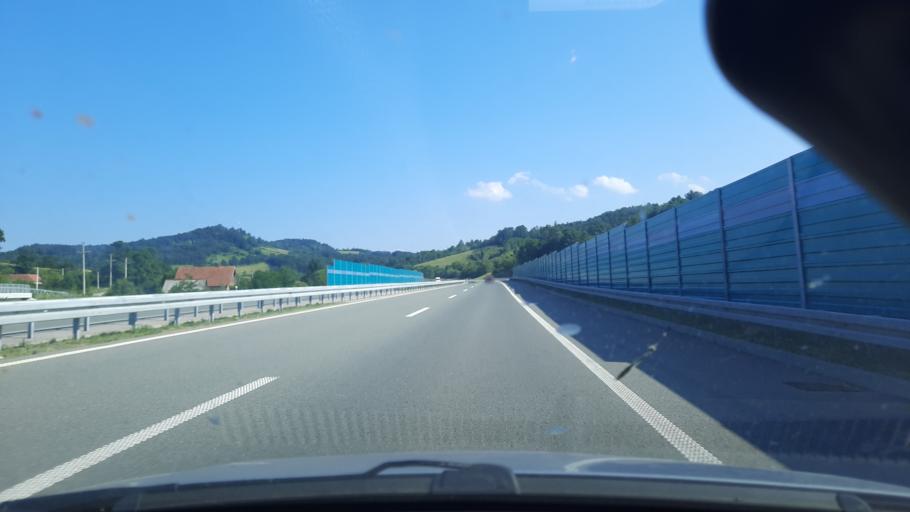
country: RS
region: Central Serbia
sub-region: Kolubarski Okrug
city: Ljig
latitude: 44.1496
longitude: 20.3314
